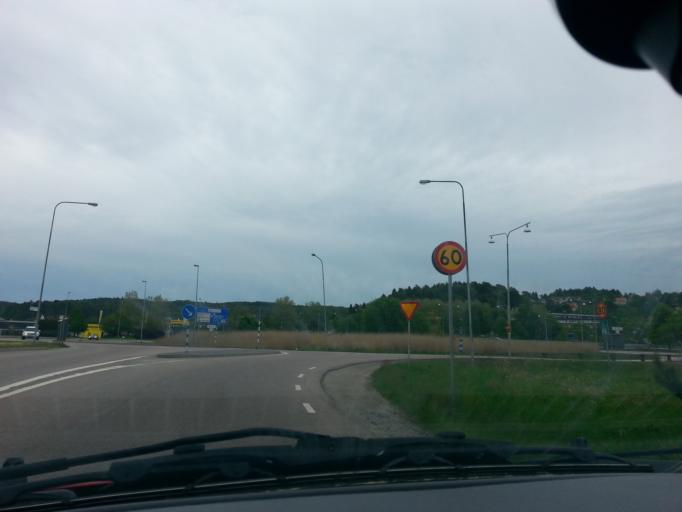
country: SE
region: Vaestra Goetaland
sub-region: Partille Kommun
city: Partille
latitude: 57.7409
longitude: 12.1236
